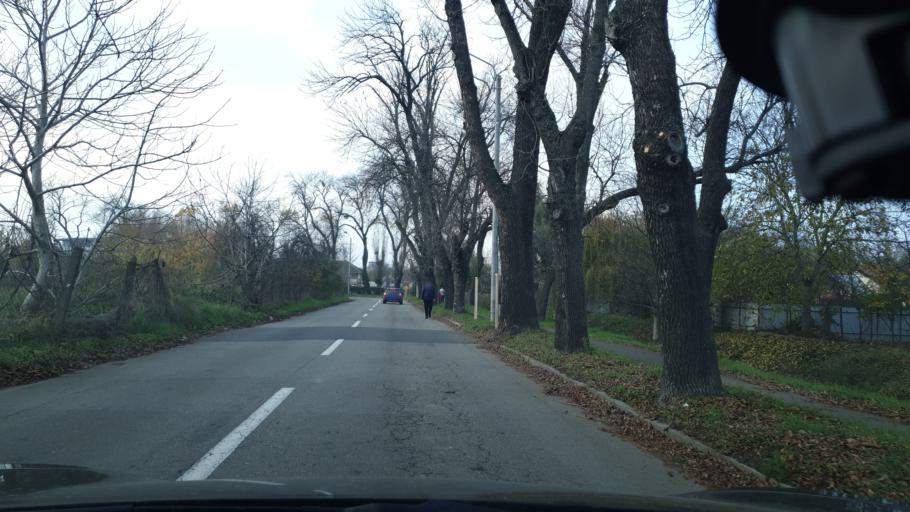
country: RO
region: Timis
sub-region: Comuna Ghiroda
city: Ghiroda
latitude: 45.7595
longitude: 21.2670
